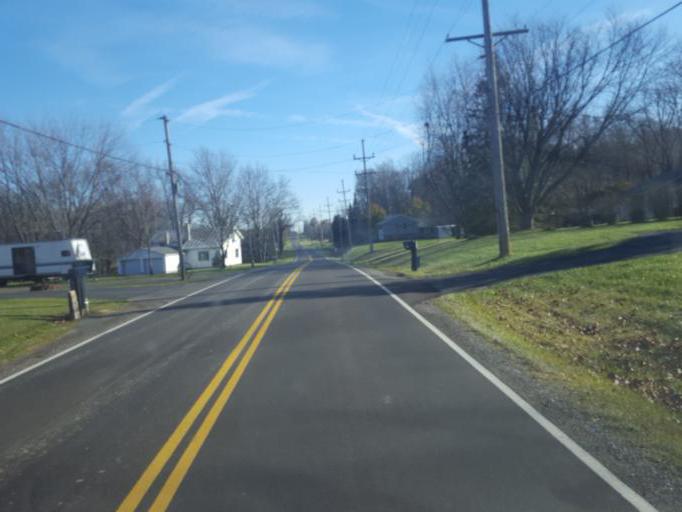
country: US
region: Ohio
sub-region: Crawford County
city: Bucyrus
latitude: 40.8270
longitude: -82.9012
